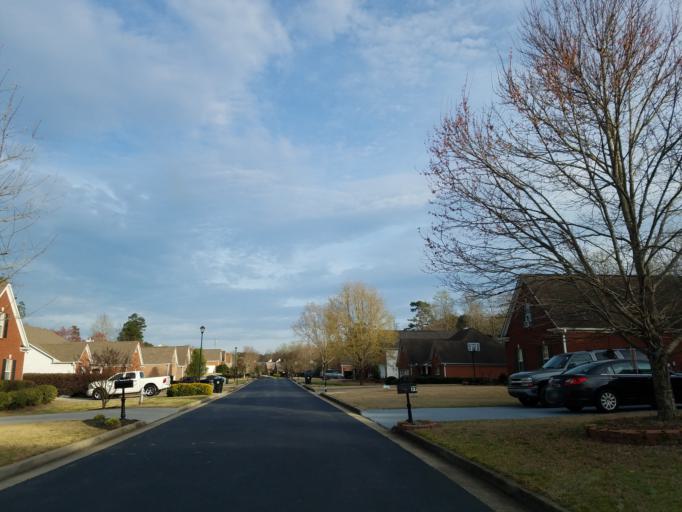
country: US
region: Georgia
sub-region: Dawson County
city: Dawsonville
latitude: 34.4291
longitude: -84.1260
